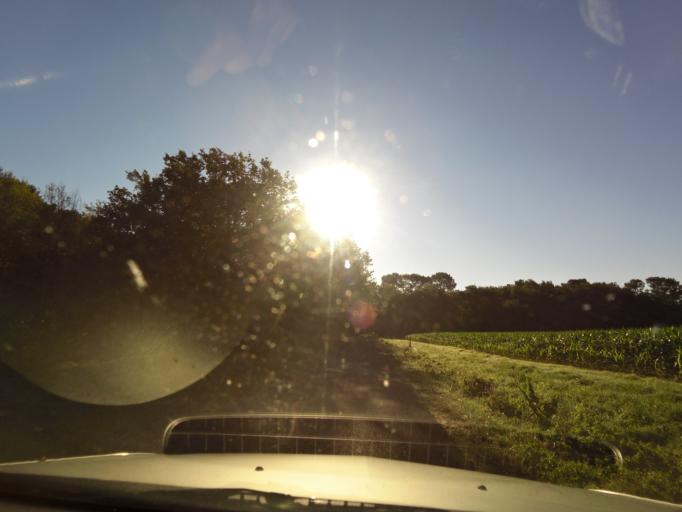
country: FR
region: Aquitaine
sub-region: Departement de la Gironde
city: Castets-en-Dorthe
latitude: 44.5066
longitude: -0.1471
